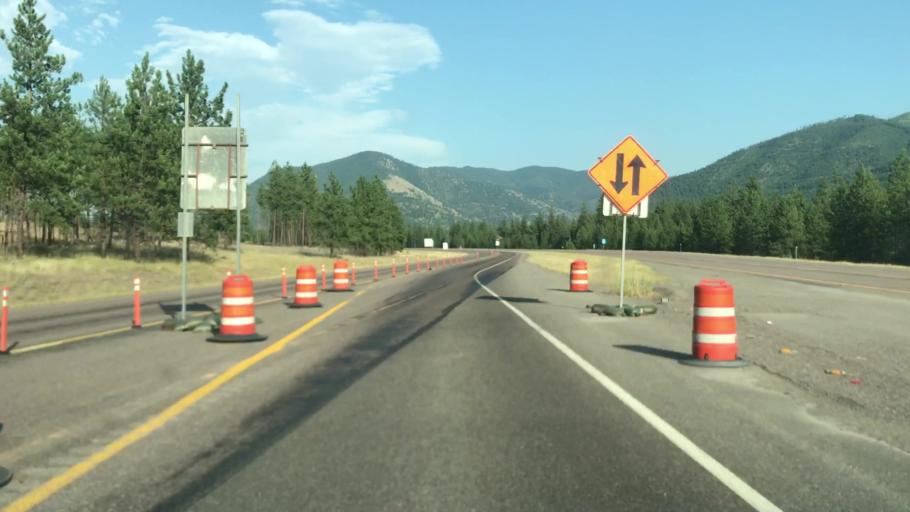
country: US
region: Montana
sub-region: Mineral County
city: Superior
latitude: 47.0133
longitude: -114.7280
